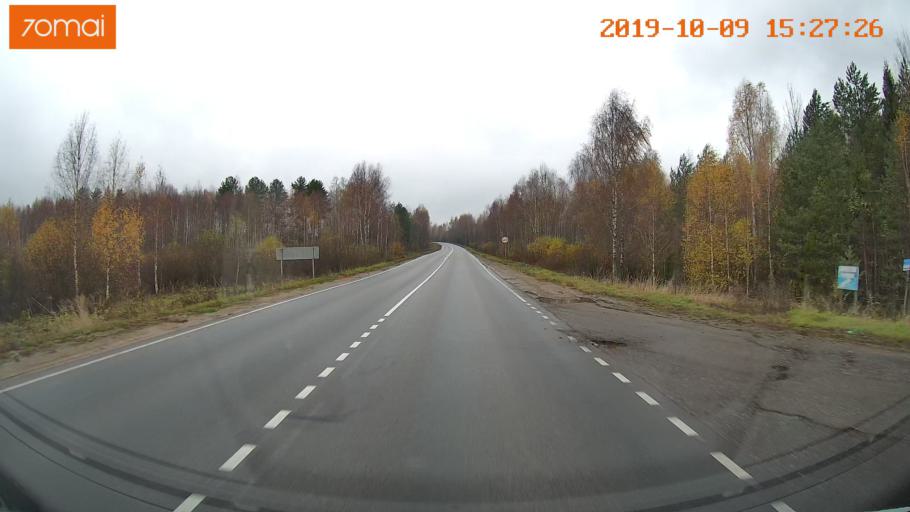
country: RU
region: Kostroma
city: Susanino
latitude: 58.0135
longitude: 41.3793
